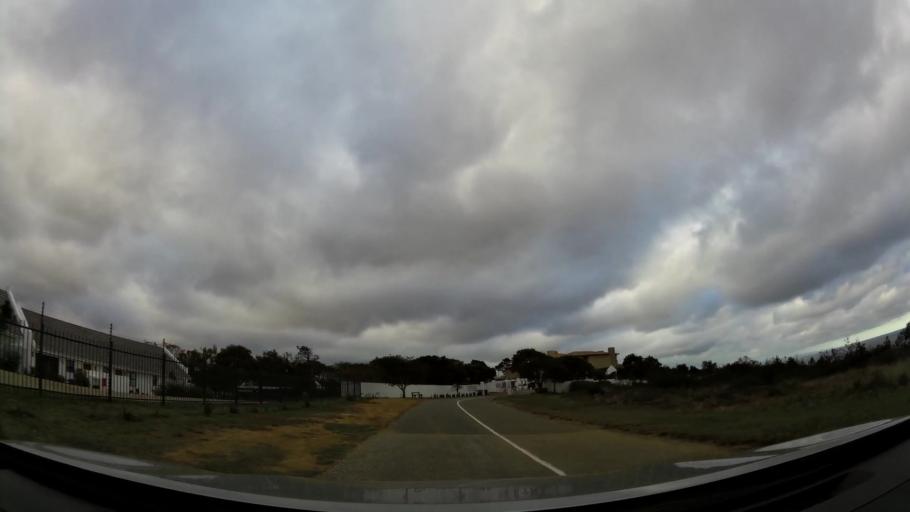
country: ZA
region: Western Cape
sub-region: Eden District Municipality
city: Plettenberg Bay
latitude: -34.0442
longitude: 23.3620
